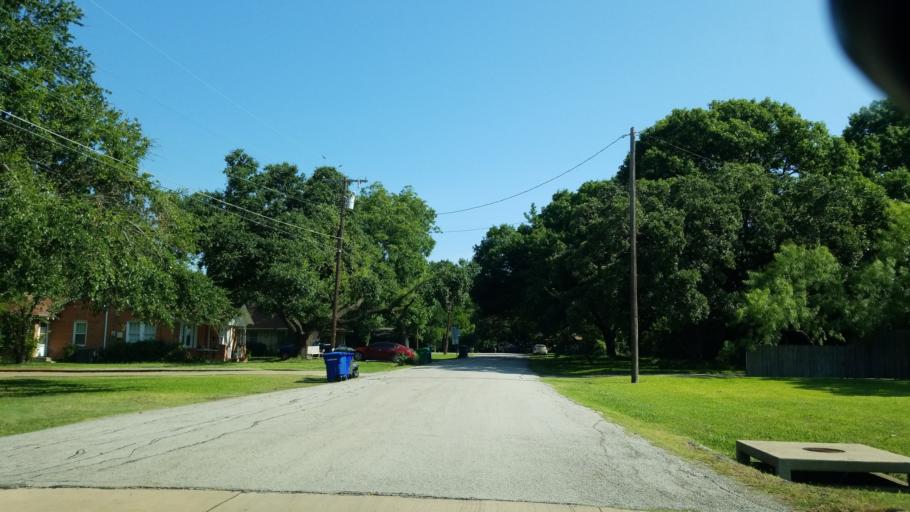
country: US
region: Texas
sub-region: Dallas County
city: Carrollton
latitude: 32.9555
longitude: -96.8980
